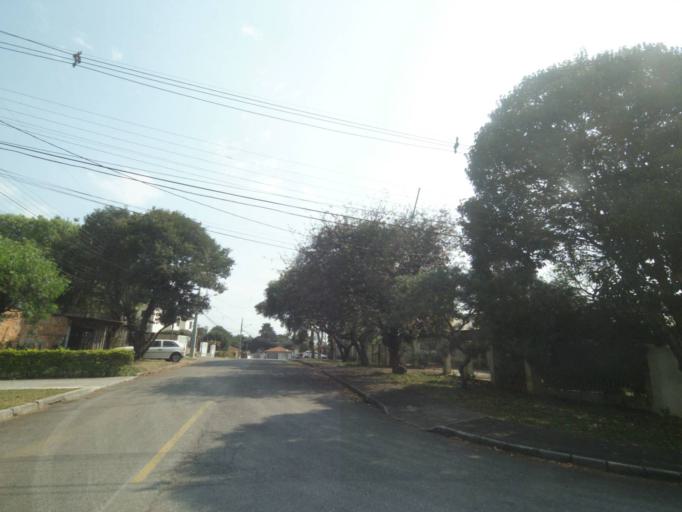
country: BR
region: Parana
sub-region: Sao Jose Dos Pinhais
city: Sao Jose dos Pinhais
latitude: -25.5066
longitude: -49.2537
